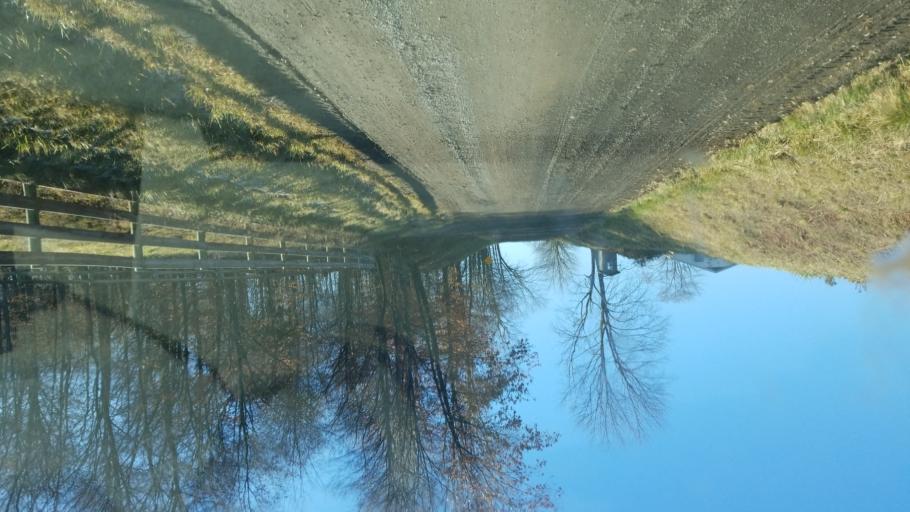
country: US
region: Ohio
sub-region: Wayne County
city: Apple Creek
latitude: 40.6527
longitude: -81.8577
